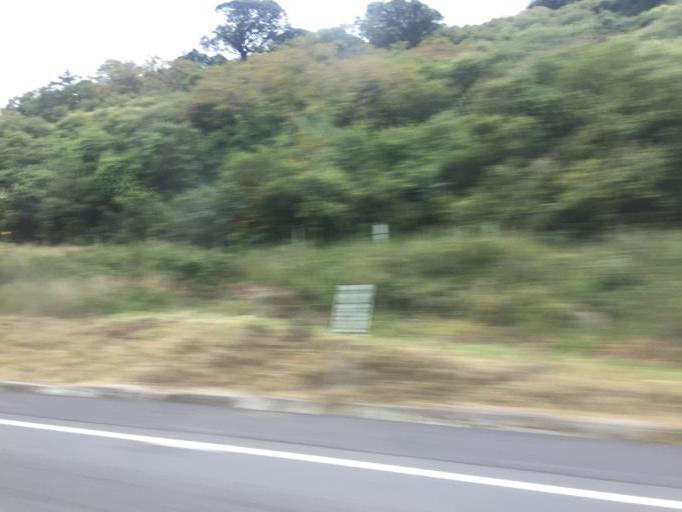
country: MX
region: Jalisco
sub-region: Zapotlan del Rey
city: Zapotlan del Rey
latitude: 20.5011
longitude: -102.9522
